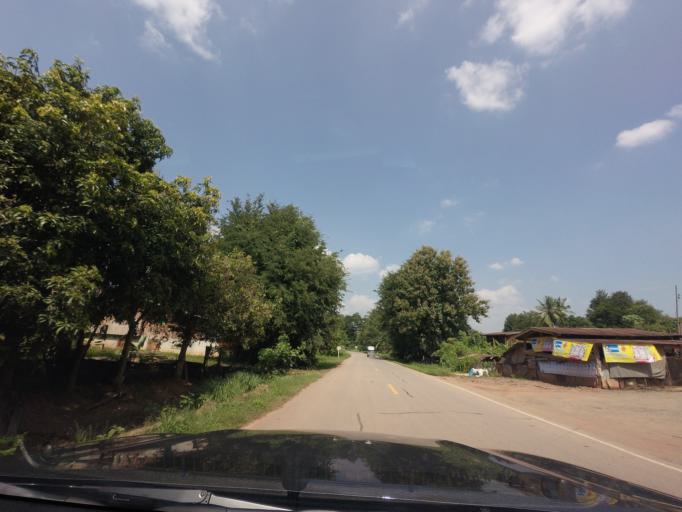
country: TH
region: Uttaradit
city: Ban Khok
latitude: 17.9777
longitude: 101.0268
